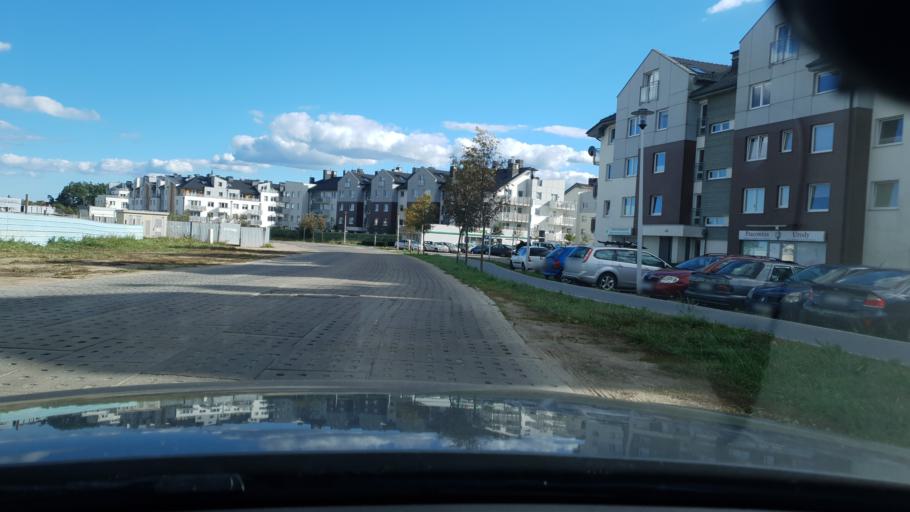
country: PL
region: Pomeranian Voivodeship
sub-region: Powiat kartuski
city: Chwaszczyno
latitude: 54.4937
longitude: 18.4320
